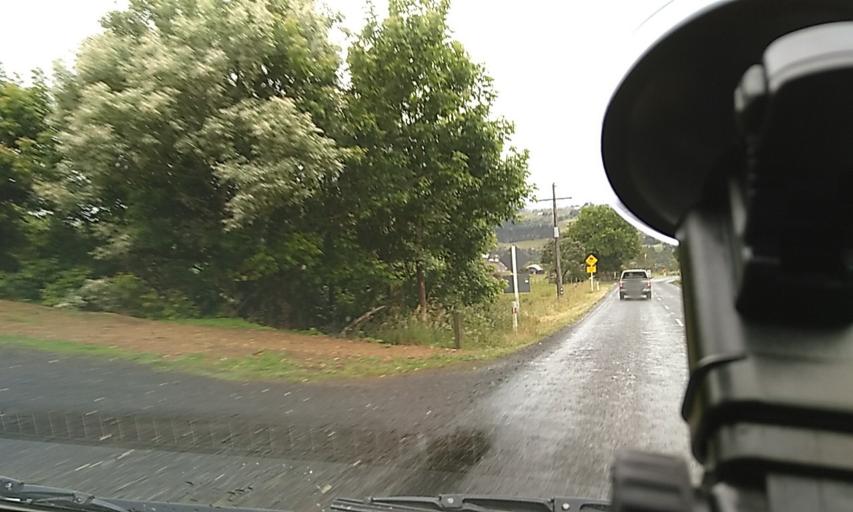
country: NZ
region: Auckland
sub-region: Auckland
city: Pukekohe East
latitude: -37.2994
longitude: 174.9366
